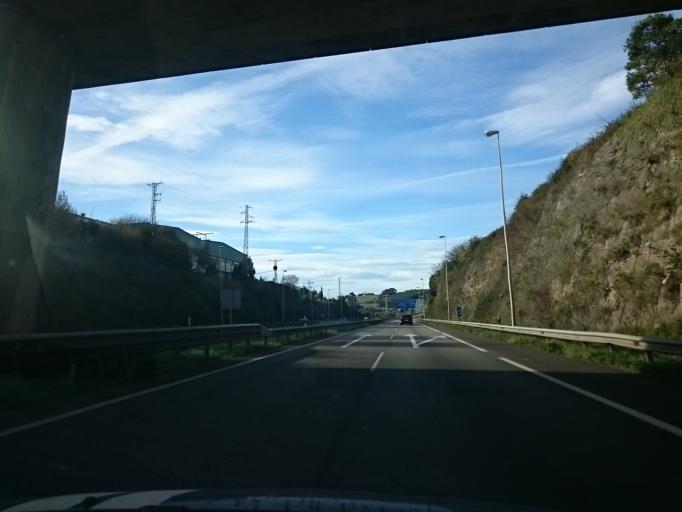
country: ES
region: Asturias
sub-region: Province of Asturias
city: Natahoyo
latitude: 43.5133
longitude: -5.6782
